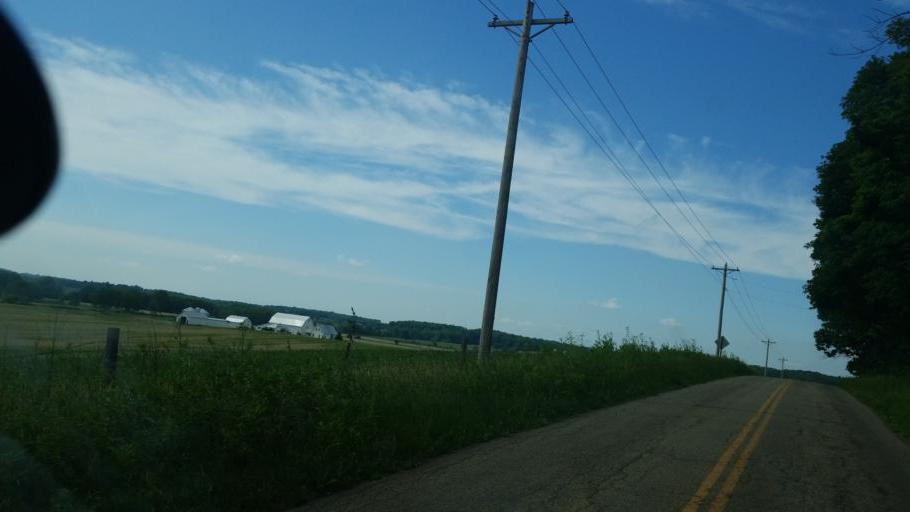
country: US
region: Ohio
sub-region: Knox County
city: Gambier
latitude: 40.2998
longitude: -82.3586
